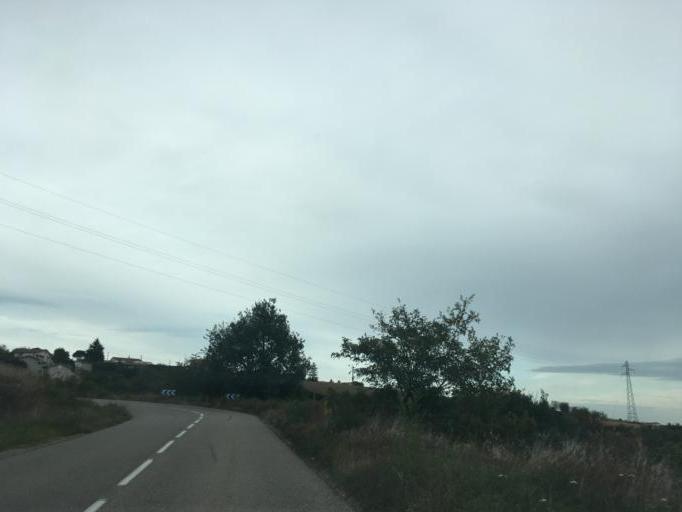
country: FR
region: Rhone-Alpes
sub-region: Departement de la Loire
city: Saint-Martin-la-Plaine
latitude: 45.5397
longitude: 4.5998
